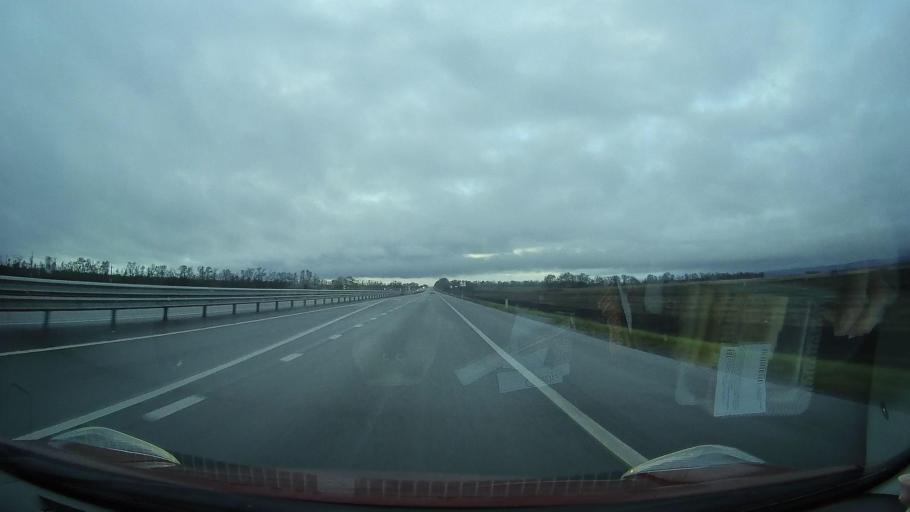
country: RU
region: Stavropol'skiy
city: Zavetnoye
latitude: 44.7845
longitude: 41.5219
